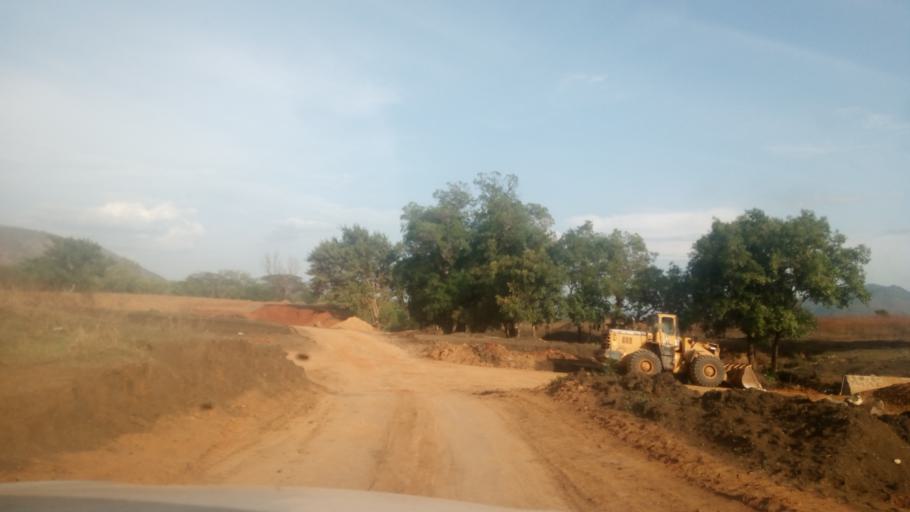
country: ET
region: Oromiya
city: Mendi
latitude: 10.2105
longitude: 35.0806
